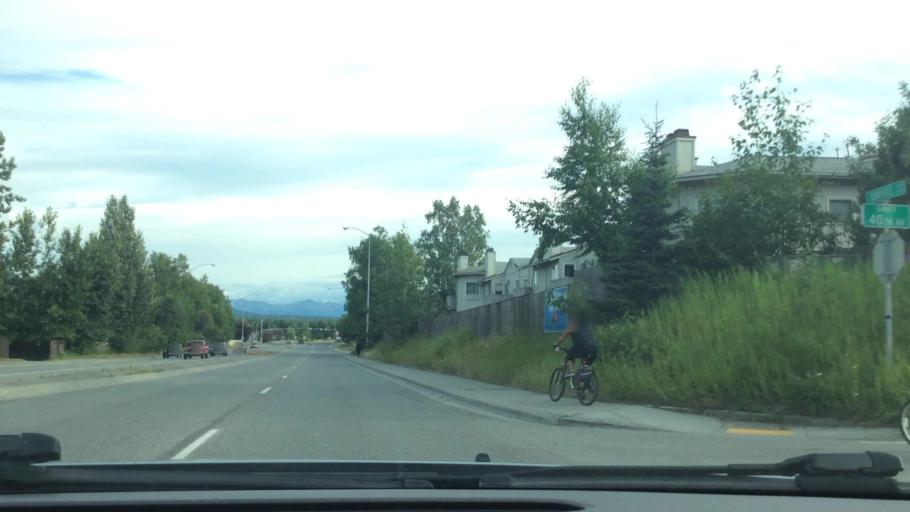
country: US
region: Alaska
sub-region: Anchorage Municipality
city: Anchorage
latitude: 61.1846
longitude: -149.7785
